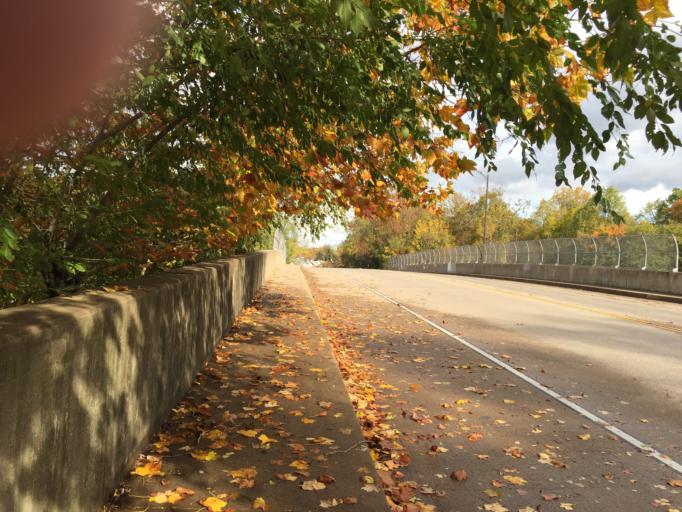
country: US
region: Virginia
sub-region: Fairfax County
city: Seven Corners
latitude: 38.8817
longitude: -77.1461
